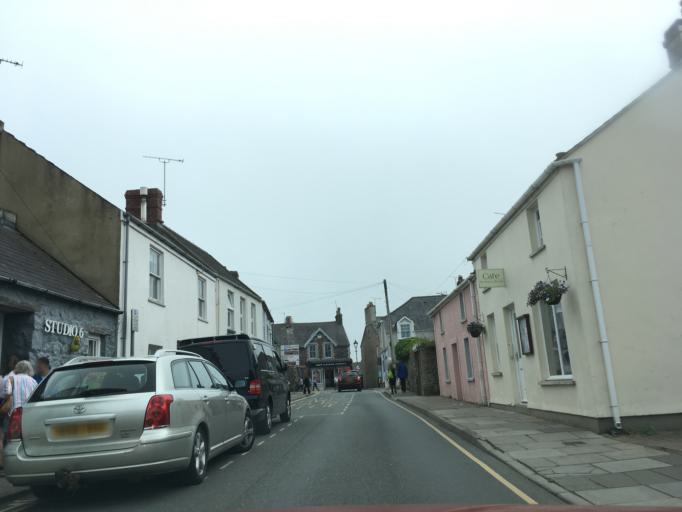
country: GB
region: Wales
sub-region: Pembrokeshire
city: Saint David's
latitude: 51.8814
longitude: -5.2643
